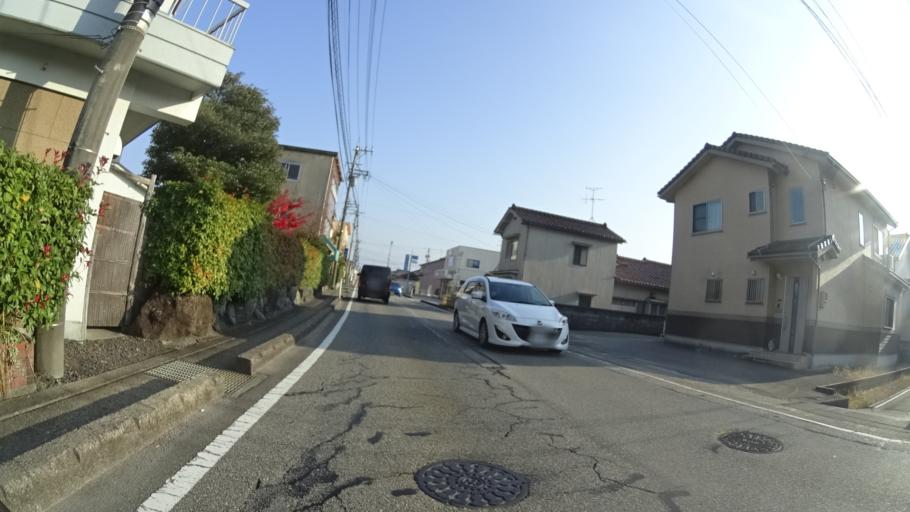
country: JP
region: Toyama
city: Toyama-shi
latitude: 36.6972
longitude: 137.2650
